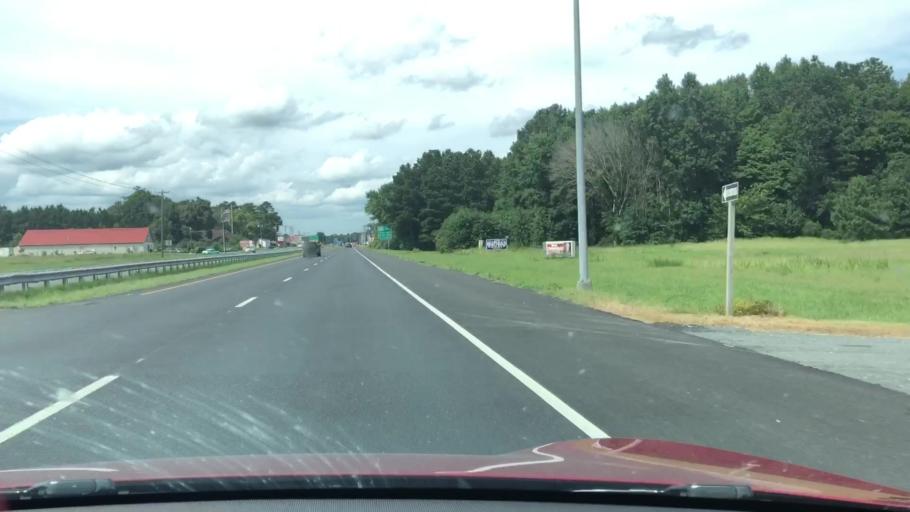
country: US
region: Maryland
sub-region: Worcester County
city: Pocomoke City
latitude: 38.0467
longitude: -75.5428
